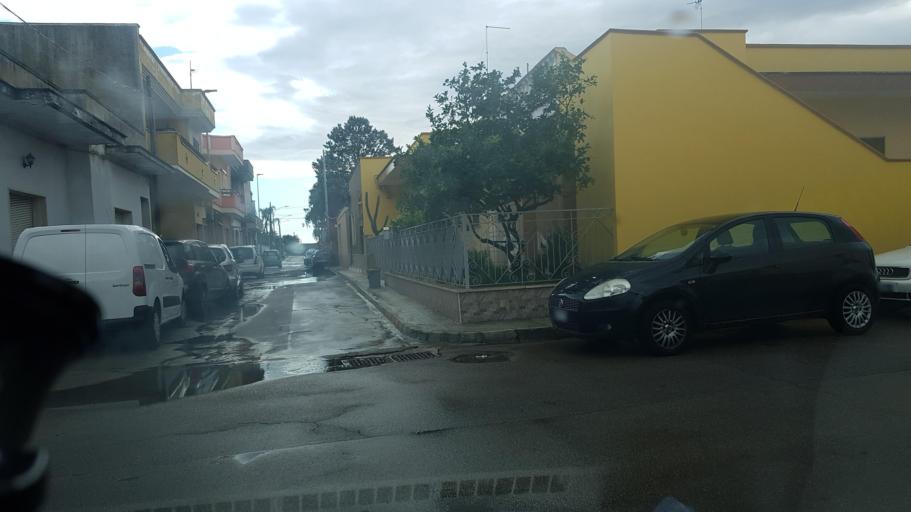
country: IT
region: Apulia
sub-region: Provincia di Lecce
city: Carmiano
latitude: 40.3401
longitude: 18.0411
